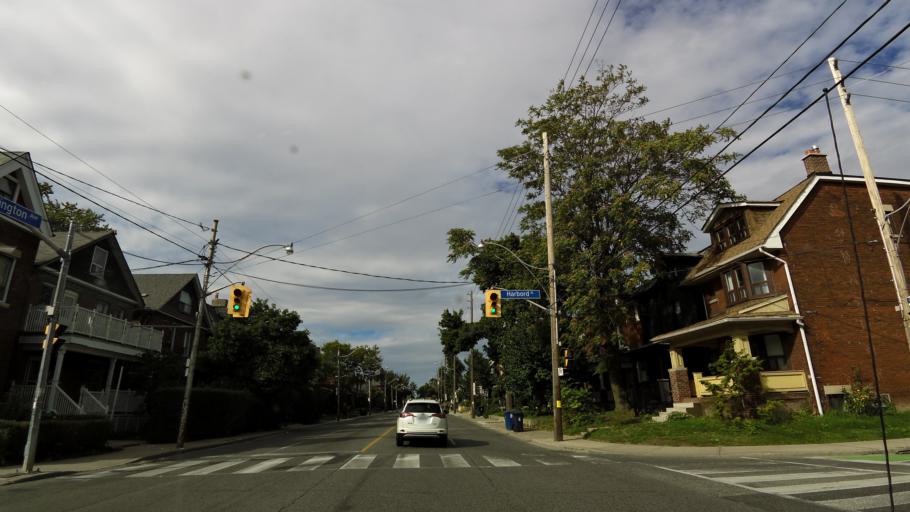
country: CA
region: Ontario
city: Toronto
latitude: 43.6584
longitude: -79.4243
